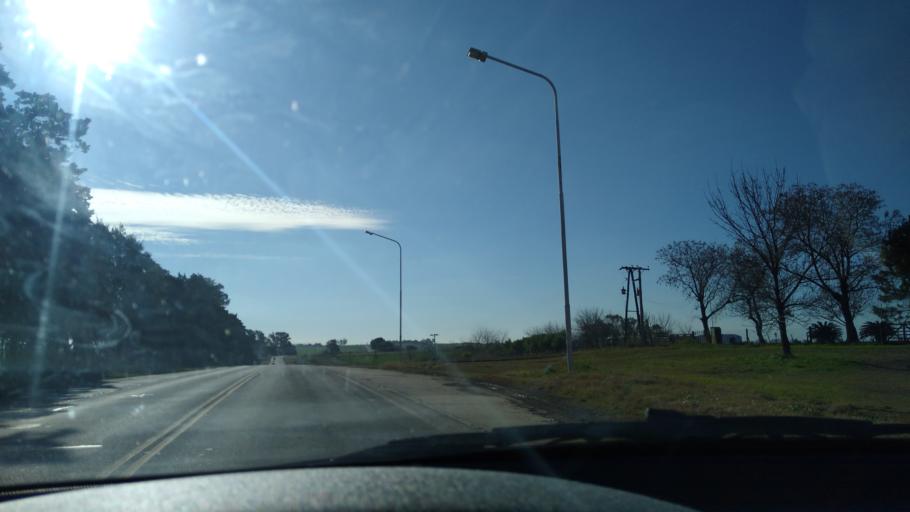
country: AR
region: Entre Rios
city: Aranguren
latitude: -32.4147
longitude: -60.3190
